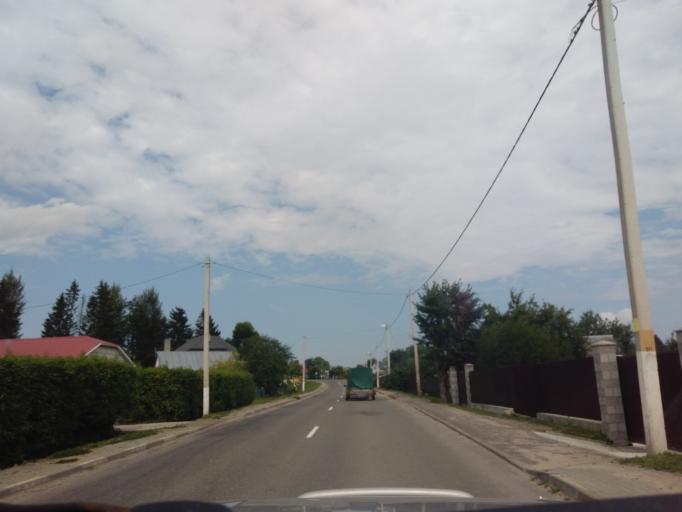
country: BY
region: Minsk
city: Khatsyezhyna
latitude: 53.9125
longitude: 27.3123
